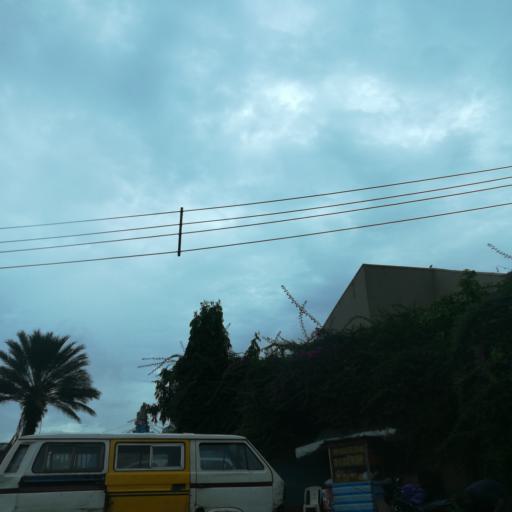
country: NG
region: Lagos
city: Oshodi
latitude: 6.5538
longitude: 3.3438
